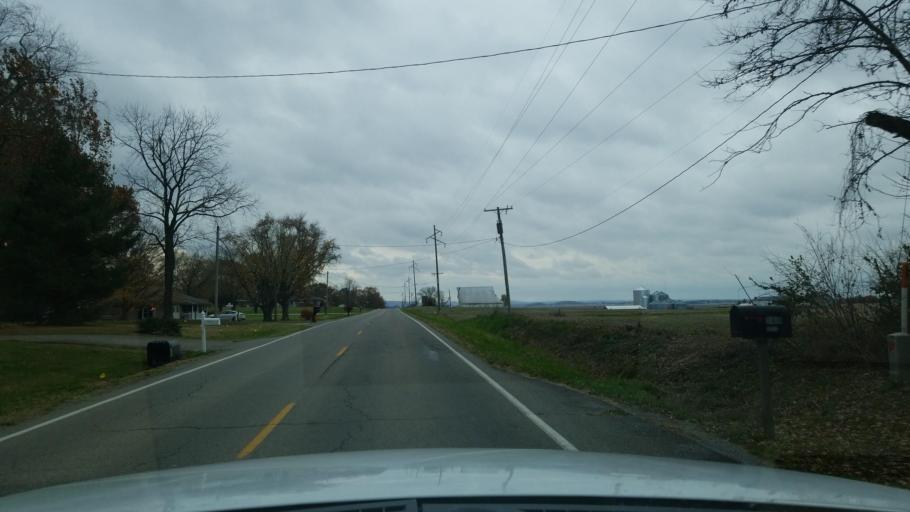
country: US
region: Illinois
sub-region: Saline County
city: Eldorado
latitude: 37.7970
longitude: -88.4383
